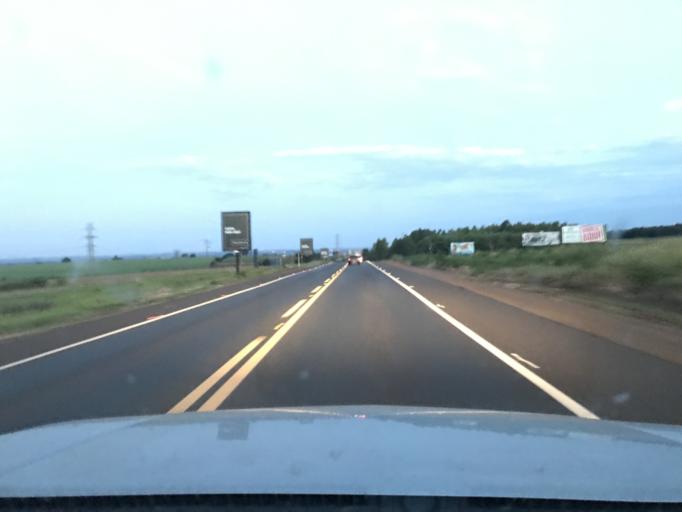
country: PY
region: Canindeyu
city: Salto del Guaira
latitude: -24.0158
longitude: -54.2986
